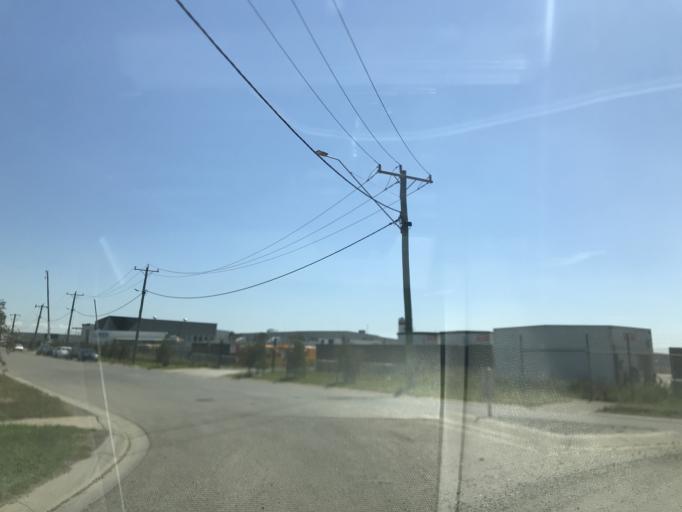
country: AU
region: Victoria
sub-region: Wyndham
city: Truganina
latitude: -37.8305
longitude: 144.7699
